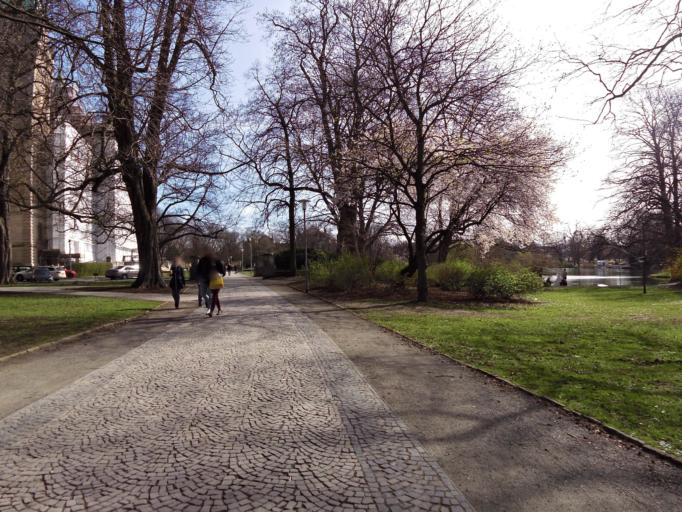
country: DE
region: Lower Saxony
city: Hannover
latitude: 52.3670
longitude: 9.7353
